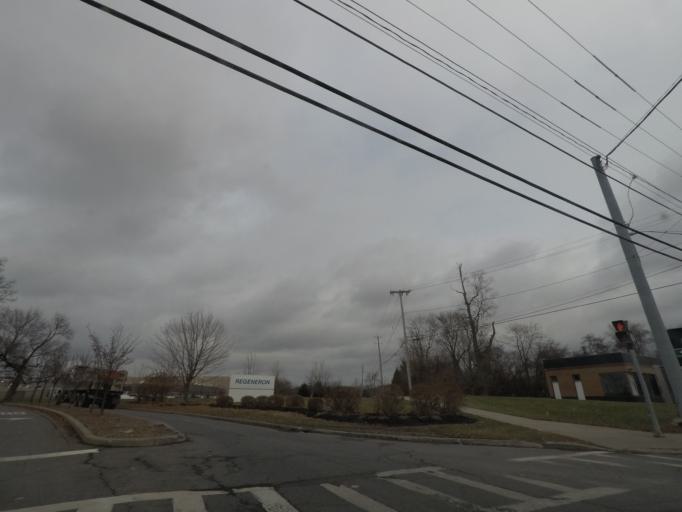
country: US
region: New York
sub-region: Rensselaer County
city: Hampton Manor
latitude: 42.6242
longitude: -73.7395
